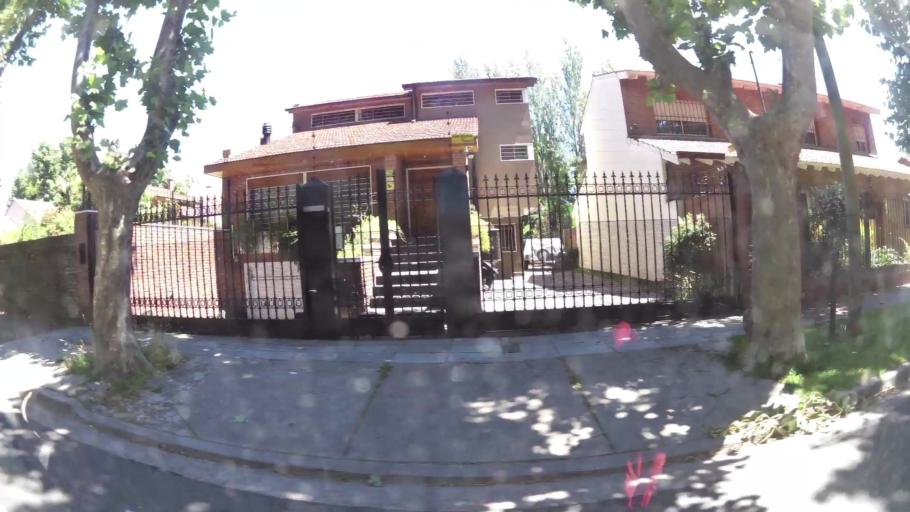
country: AR
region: Buenos Aires
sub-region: Partido de San Isidro
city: San Isidro
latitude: -34.5137
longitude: -58.5437
